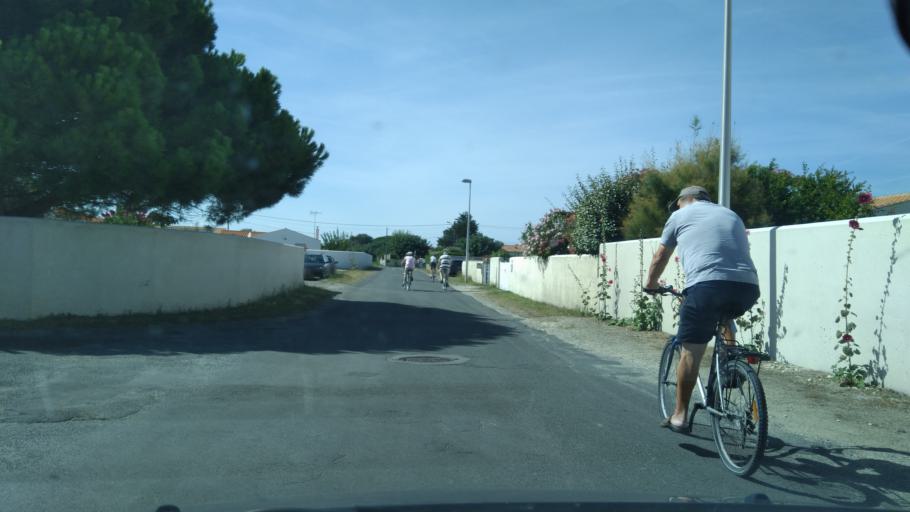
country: FR
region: Poitou-Charentes
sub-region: Departement de la Charente-Maritime
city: Dolus-d'Oleron
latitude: 45.9206
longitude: -1.3314
